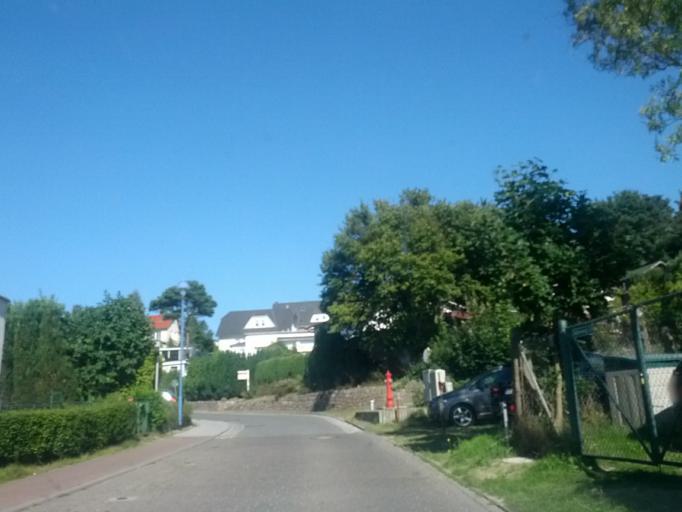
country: DE
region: Mecklenburg-Vorpommern
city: Ostseebad Gohren
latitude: 54.3407
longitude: 13.7344
